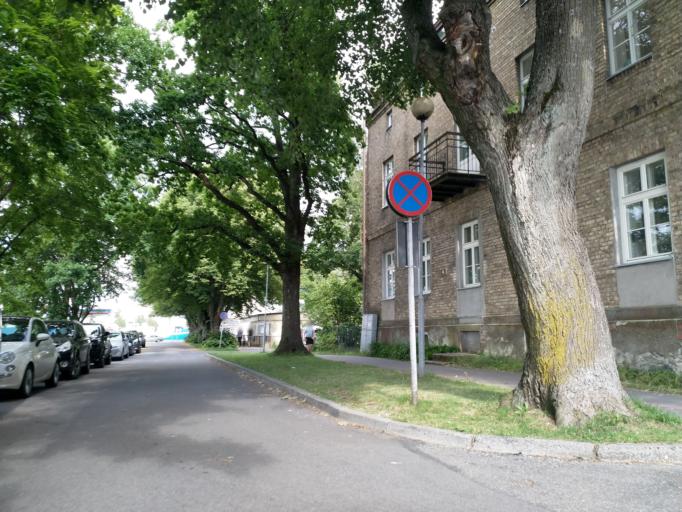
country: EE
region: Paernumaa
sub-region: Paernu linn
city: Parnu
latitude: 58.3864
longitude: 24.4894
